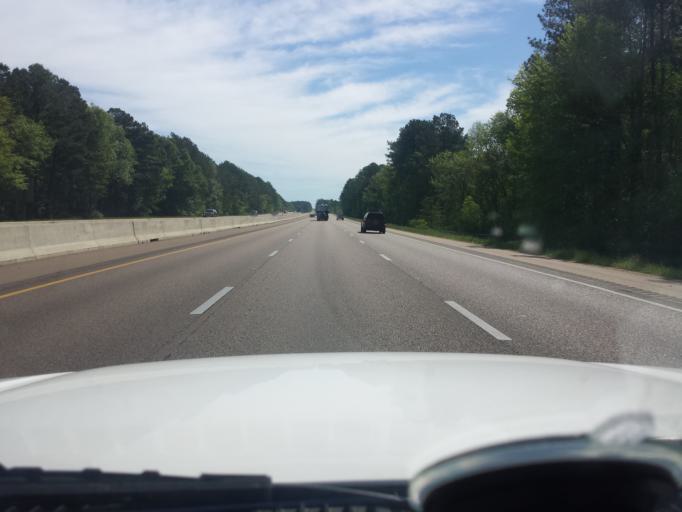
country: US
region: Mississippi
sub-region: Rankin County
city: Pearl
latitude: 32.2664
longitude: -90.1249
